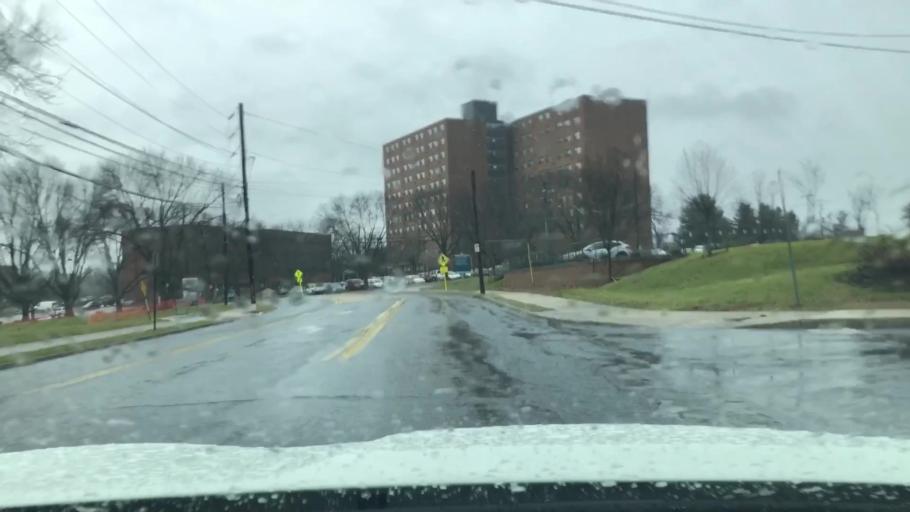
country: US
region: Pennsylvania
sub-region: Northampton County
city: Bethlehem
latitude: 40.6428
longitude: -75.4073
